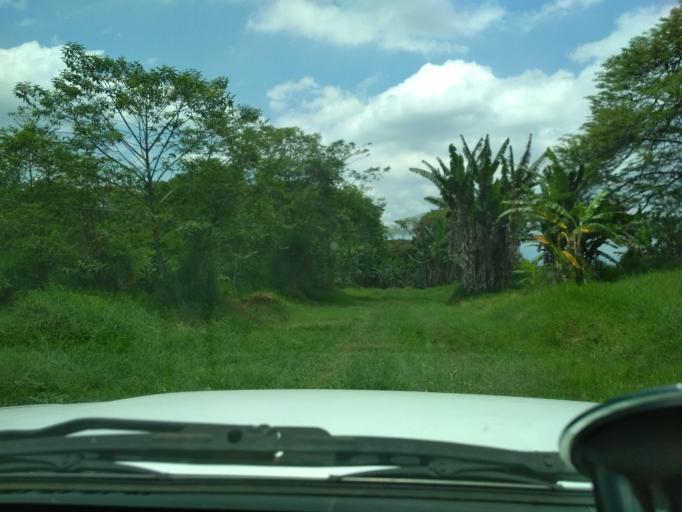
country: MX
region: Veracruz
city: Tocuila
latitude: 18.9460
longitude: -97.0149
